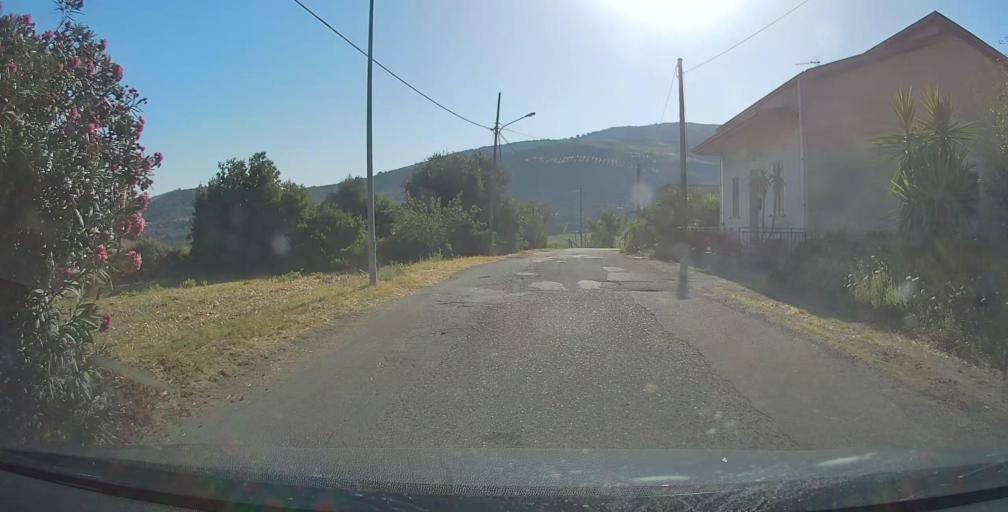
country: IT
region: Sicily
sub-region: Messina
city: San Piero Patti
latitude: 38.0752
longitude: 14.9850
